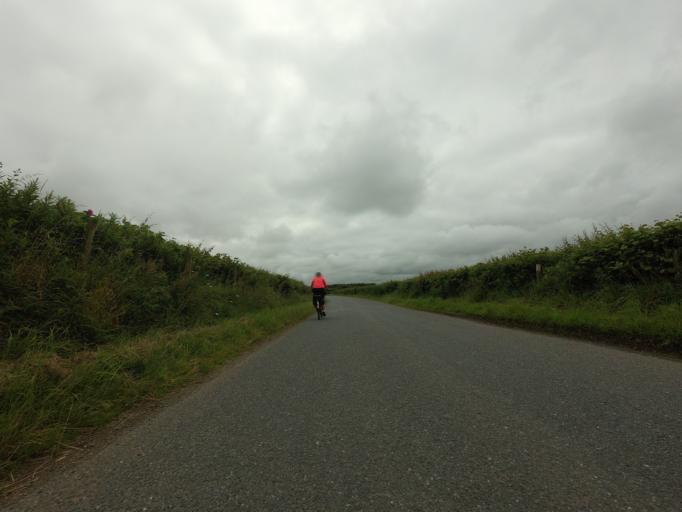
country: GB
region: Scotland
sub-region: Aberdeenshire
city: Rosehearty
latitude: 57.5362
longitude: -2.1822
